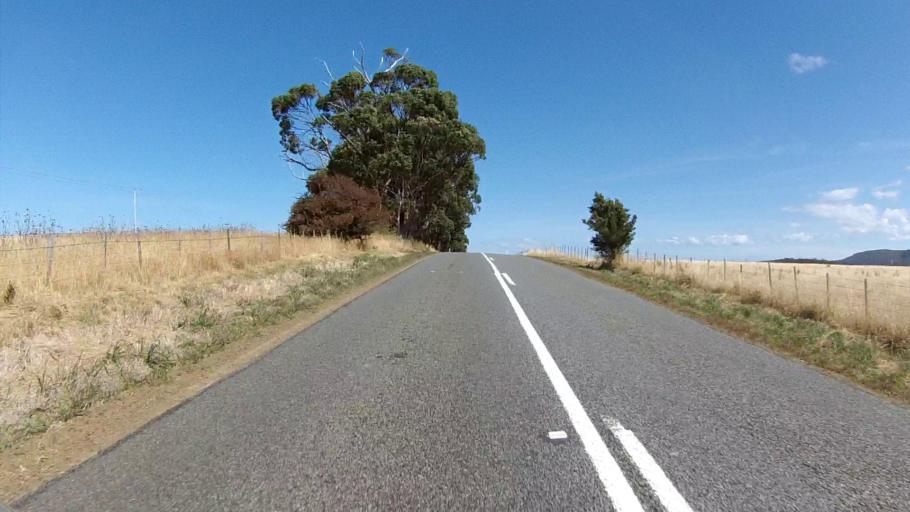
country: AU
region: Tasmania
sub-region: Sorell
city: Sorell
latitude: -42.2502
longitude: 148.0079
